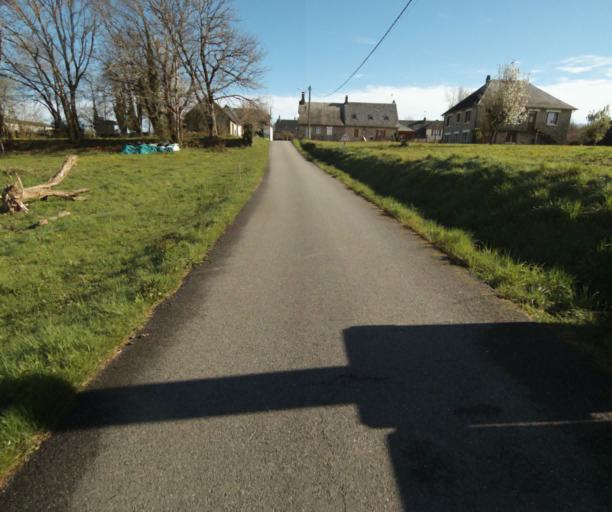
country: FR
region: Limousin
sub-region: Departement de la Correze
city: Laguenne
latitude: 45.2651
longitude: 1.8567
